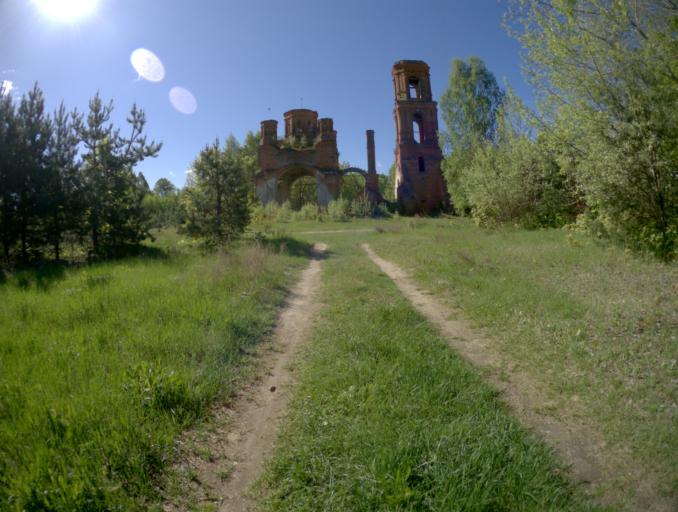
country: RU
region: Rjazan
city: Spas-Klepiki
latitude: 55.2540
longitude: 40.1135
